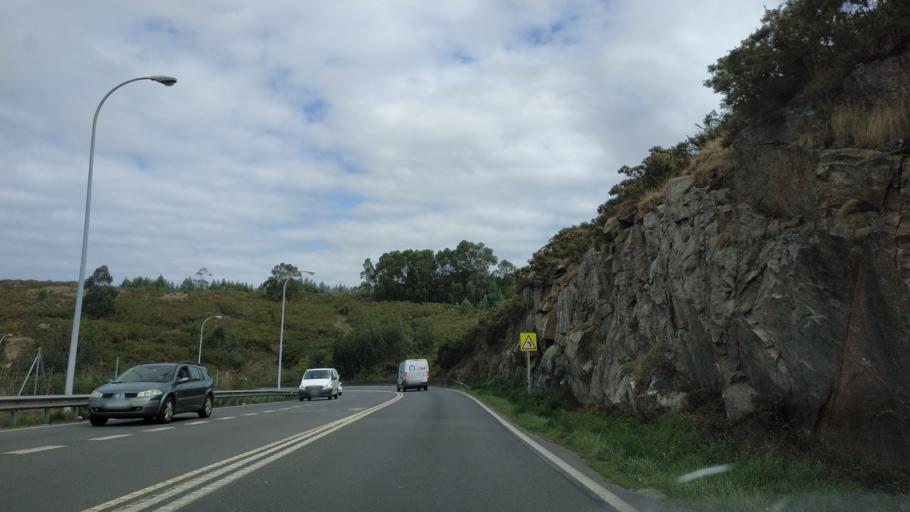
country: ES
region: Galicia
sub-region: Provincia da Coruna
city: Arteixo
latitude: 43.3334
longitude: -8.4536
